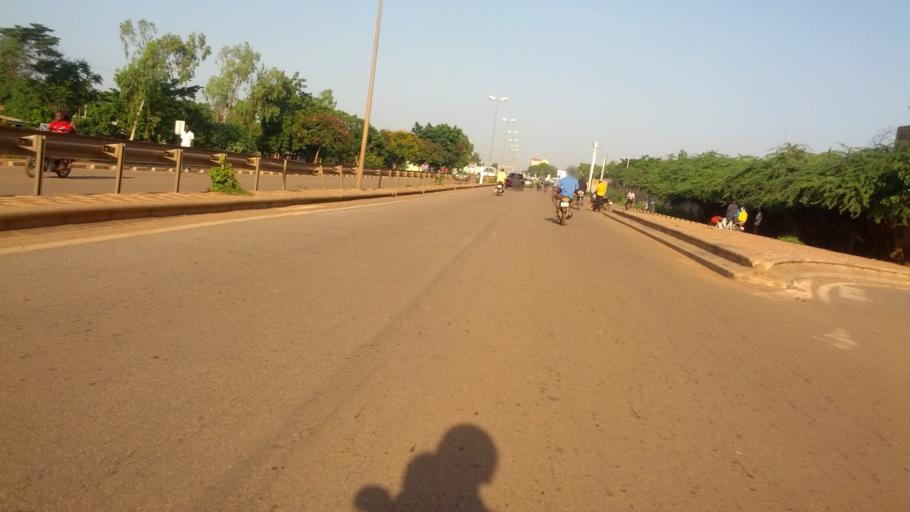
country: BF
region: Centre
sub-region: Kadiogo Province
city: Ouagadougou
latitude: 12.3330
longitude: -1.5078
